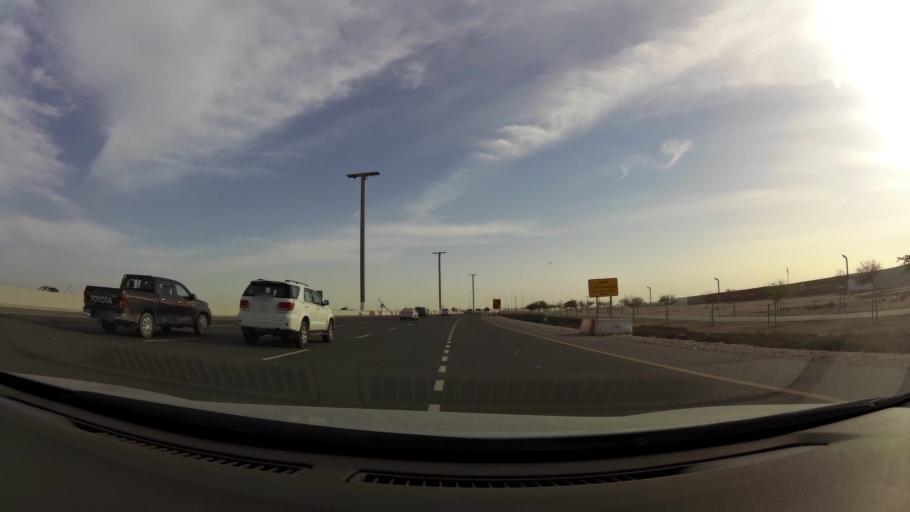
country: QA
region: Al Wakrah
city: Al Wakrah
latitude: 25.2310
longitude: 51.5925
